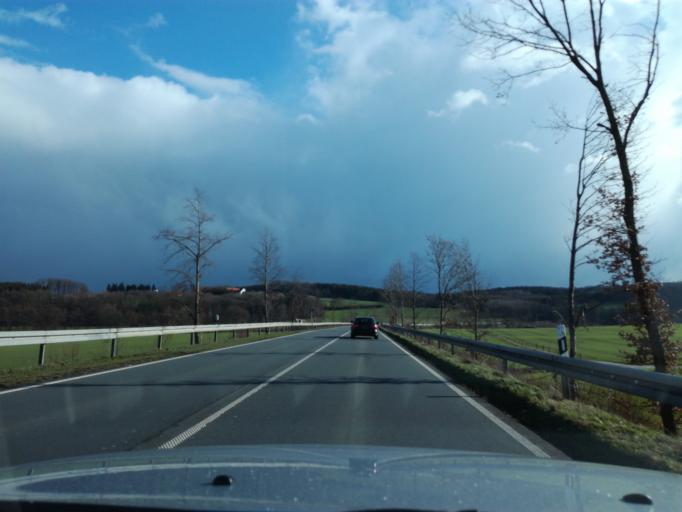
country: DE
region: North Rhine-Westphalia
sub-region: Regierungsbezirk Arnsberg
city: Menden
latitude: 51.4259
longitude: 7.7281
